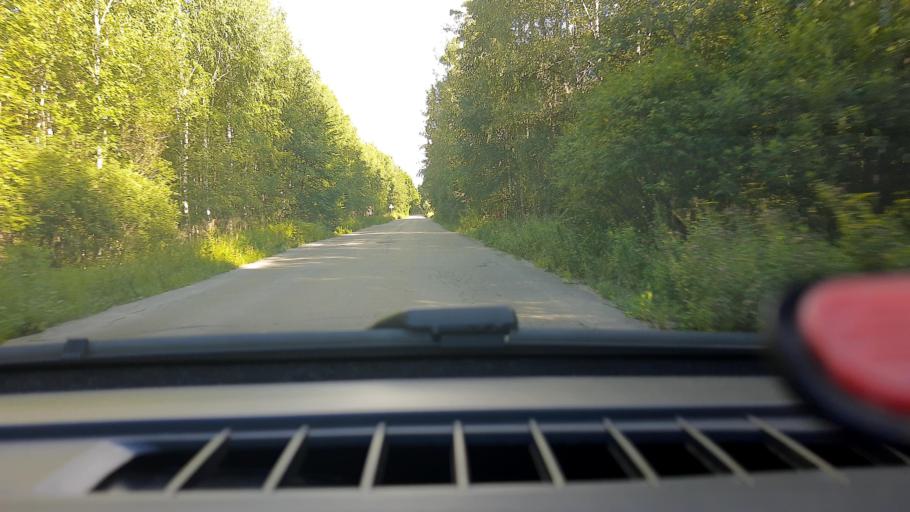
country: RU
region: Nizjnij Novgorod
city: Babino
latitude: 56.3156
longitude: 43.6238
